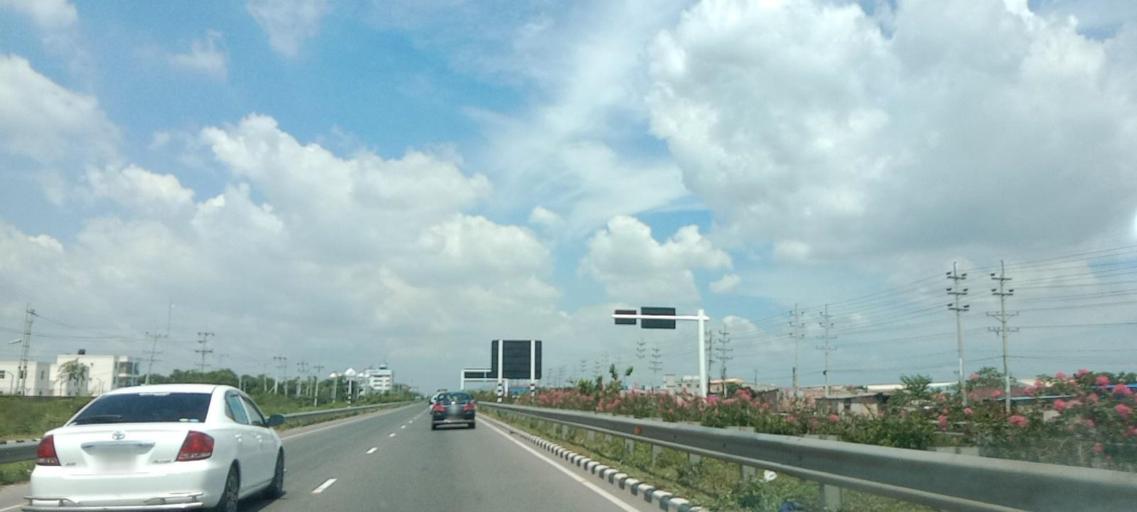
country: BD
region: Dhaka
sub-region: Dhaka
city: Dhaka
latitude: 23.6613
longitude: 90.3667
